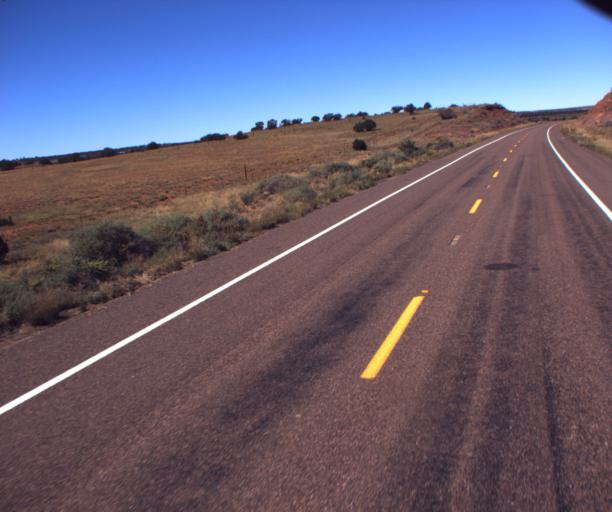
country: US
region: Arizona
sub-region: Apache County
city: Saint Johns
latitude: 34.6028
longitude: -109.6420
